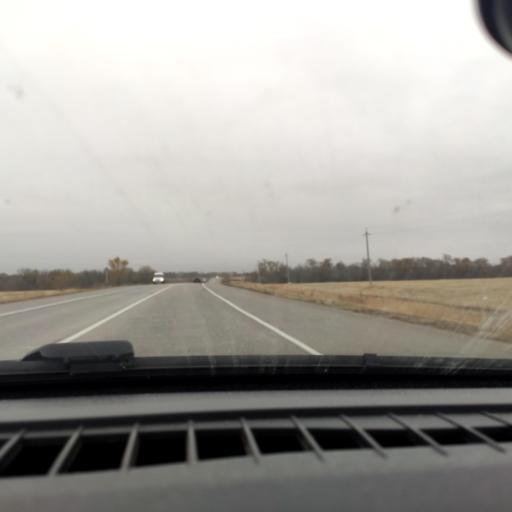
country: RU
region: Voronezj
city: Devitsa
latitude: 51.5755
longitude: 38.9749
